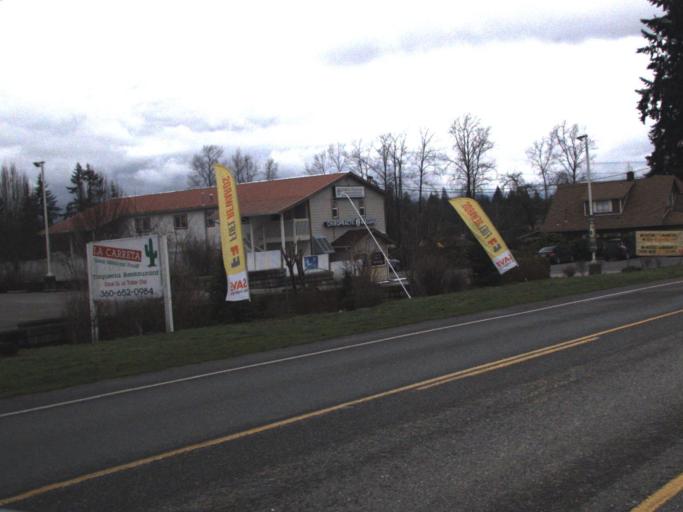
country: US
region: Washington
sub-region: Snohomish County
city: Smokey Point
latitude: 48.1519
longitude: -122.2105
